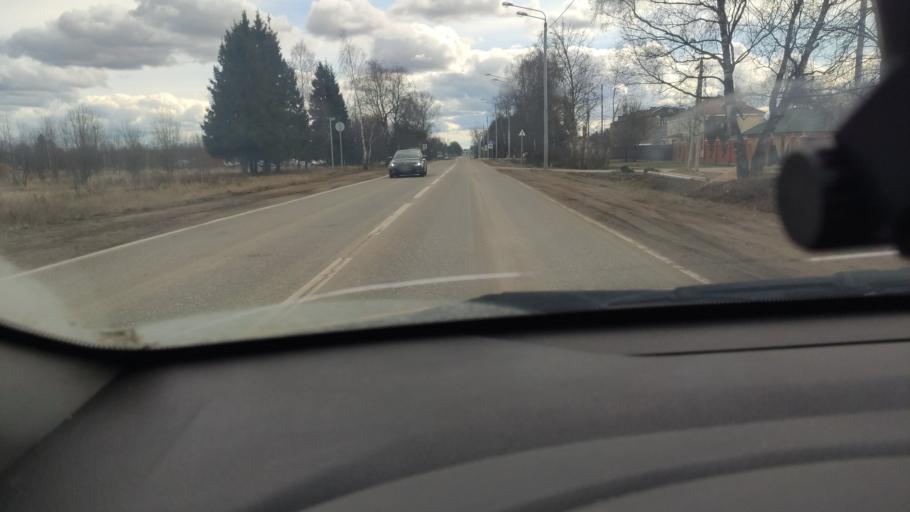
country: RU
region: Moskovskaya
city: Ruza
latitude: 55.7140
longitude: 36.1738
